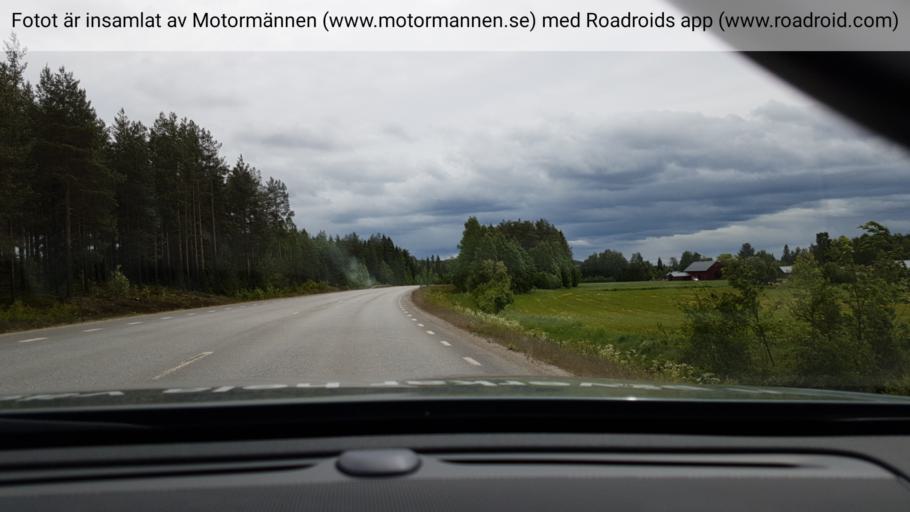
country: SE
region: Vaesterbotten
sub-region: Vannas Kommun
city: Vaennaes
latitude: 64.0059
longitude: 19.7172
